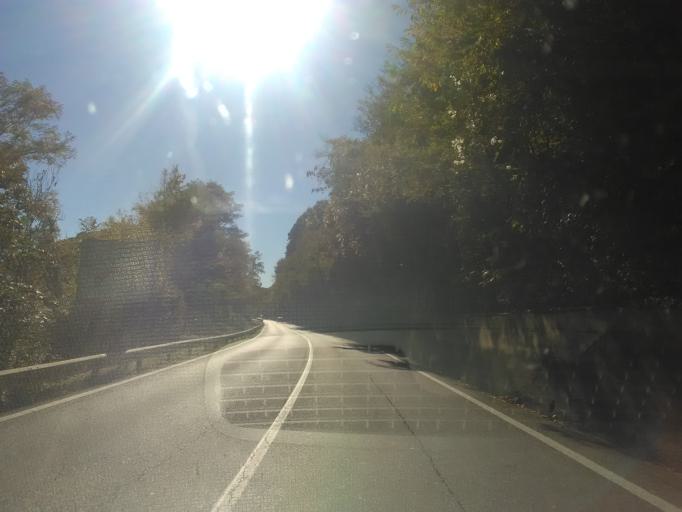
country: IT
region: Piedmont
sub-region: Provincia di Vercelli
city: Quarona
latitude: 45.7519
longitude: 8.2591
